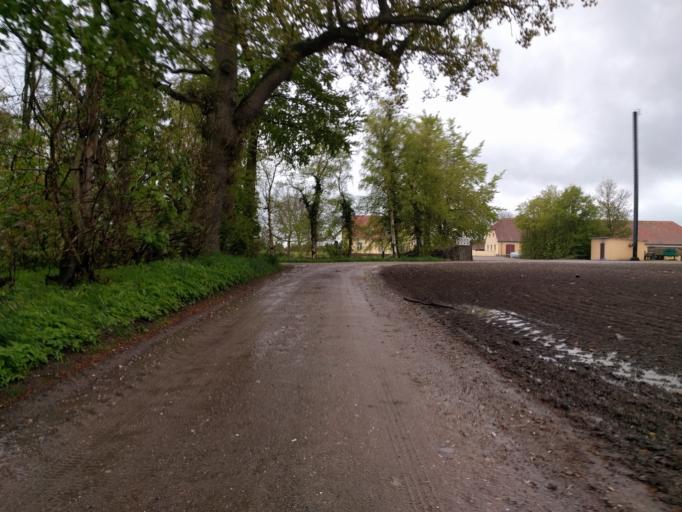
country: DK
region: South Denmark
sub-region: Kerteminde Kommune
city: Munkebo
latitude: 55.4276
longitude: 10.6021
